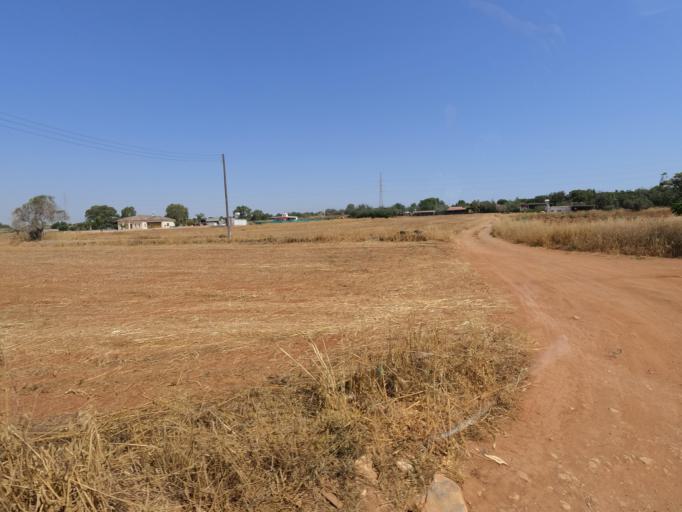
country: CY
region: Ammochostos
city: Frenaros
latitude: 35.0011
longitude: 33.9506
